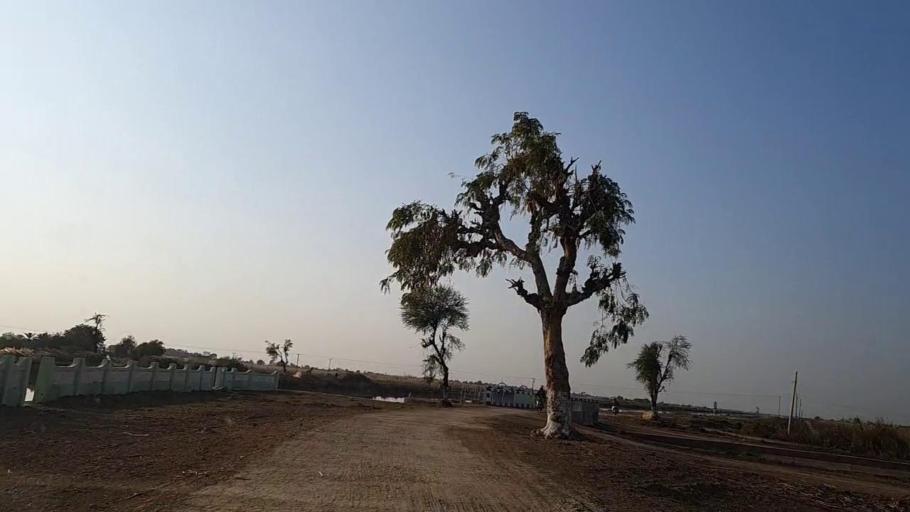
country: PK
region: Sindh
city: Sakrand
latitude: 26.0944
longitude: 68.3727
